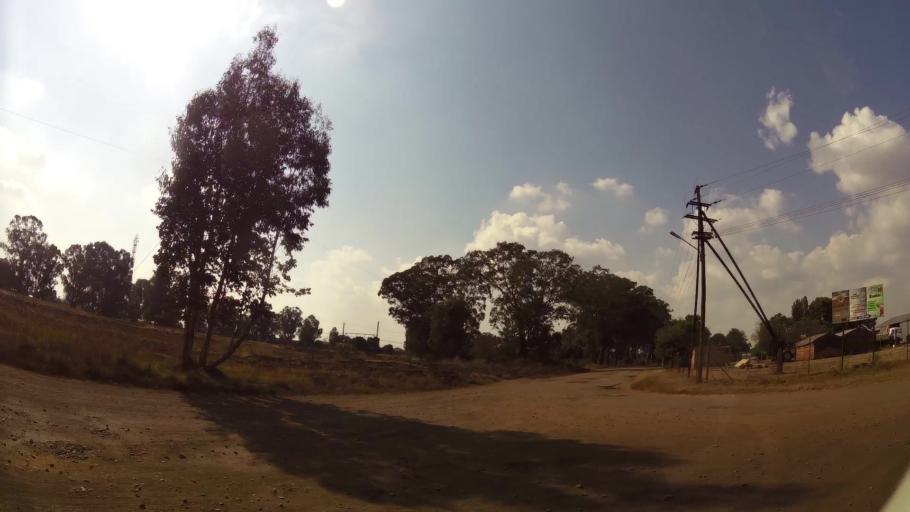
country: ZA
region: Mpumalanga
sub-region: Nkangala District Municipality
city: Delmas
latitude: -26.1885
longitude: 28.5452
